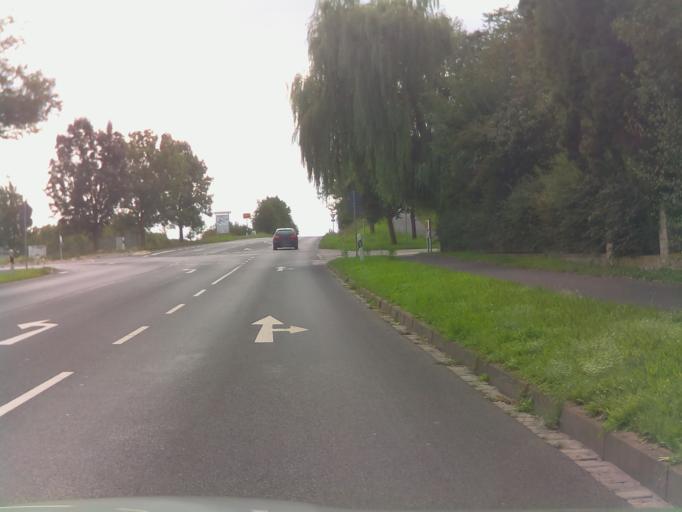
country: DE
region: Bavaria
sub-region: Regierungsbezirk Unterfranken
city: Werneck
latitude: 49.9819
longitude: 10.0924
